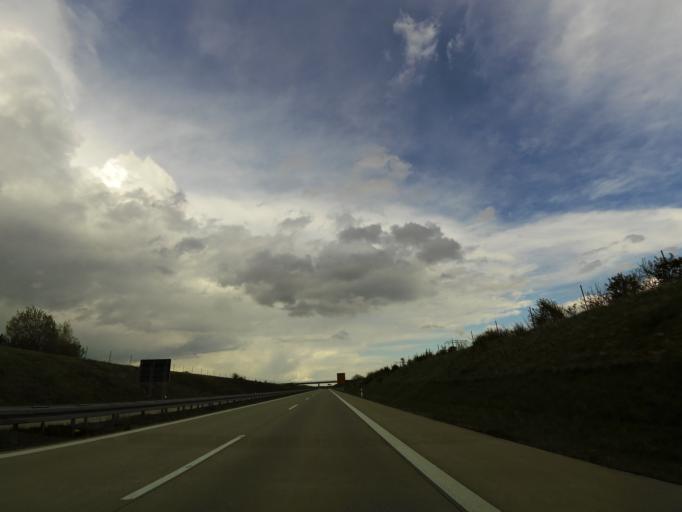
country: DE
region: Saxony-Anhalt
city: Blankenburg
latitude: 51.8049
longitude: 10.9819
